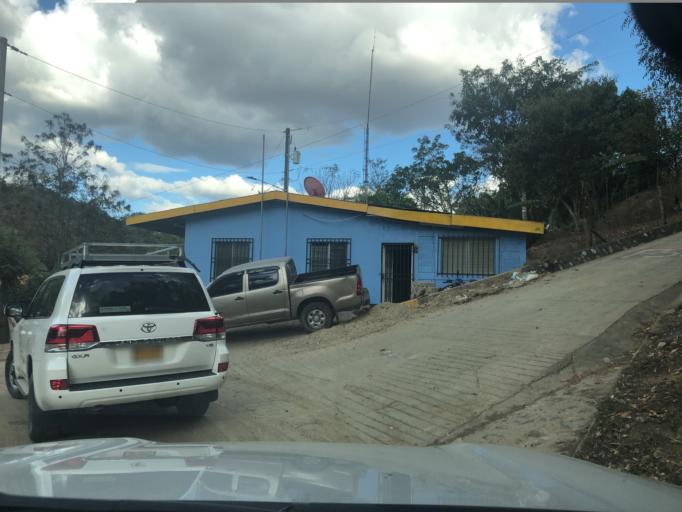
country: NI
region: Nueva Segovia
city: Ocotal
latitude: 13.6534
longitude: -86.6130
